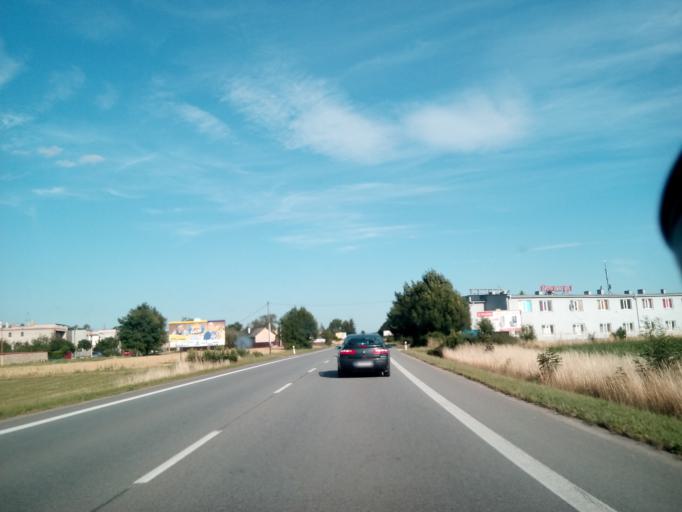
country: SK
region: Kosicky
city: Moldava nad Bodvou
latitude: 48.6093
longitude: 20.9457
